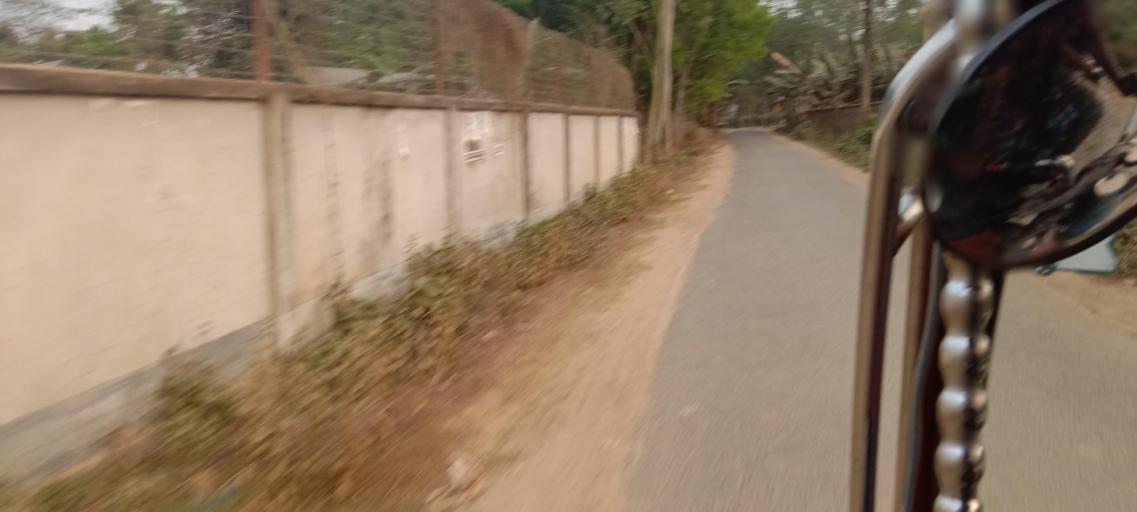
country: BD
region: Dhaka
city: Sakhipur
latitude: 24.4302
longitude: 90.2638
